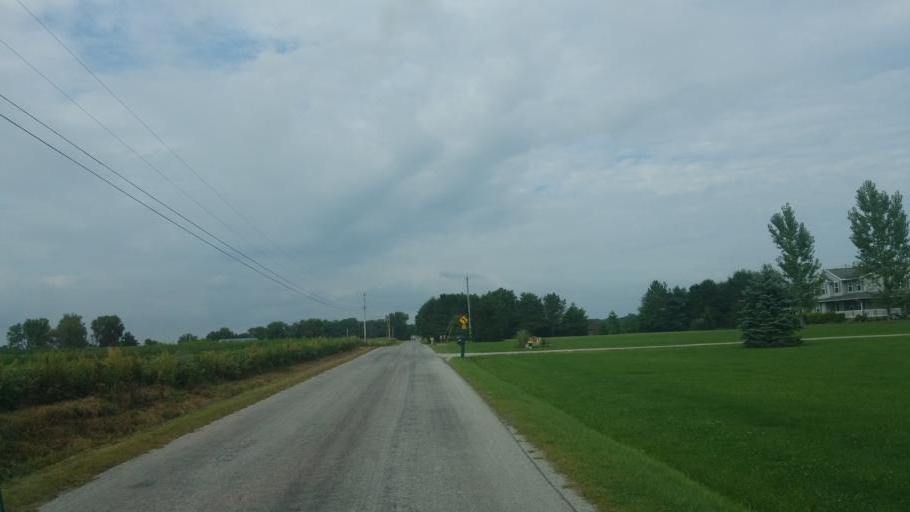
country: US
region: Ohio
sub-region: Wayne County
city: West Salem
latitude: 40.9488
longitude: -82.0554
